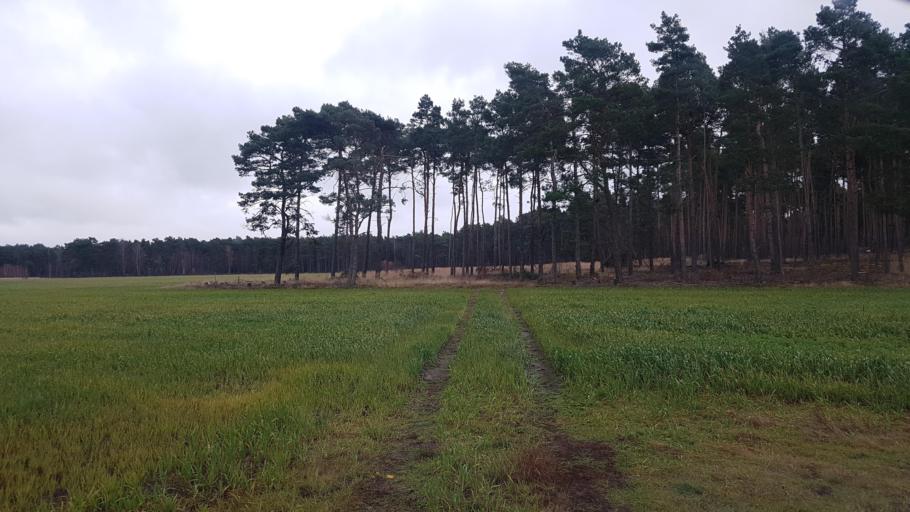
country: DE
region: Brandenburg
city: Schonewalde
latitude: 51.6453
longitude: 13.6177
